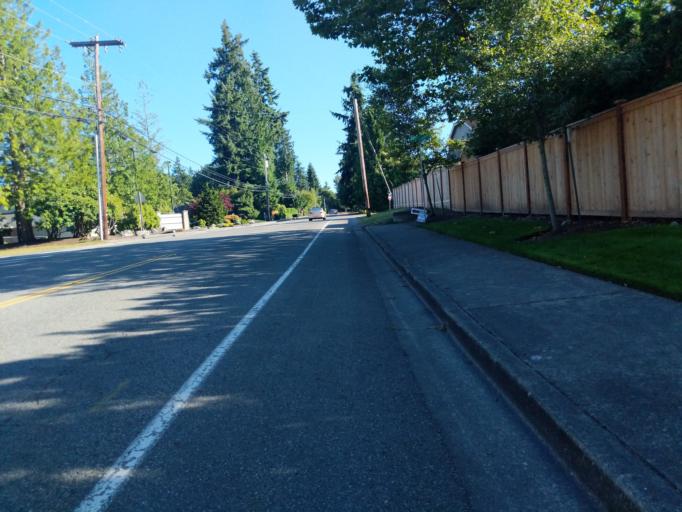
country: US
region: Washington
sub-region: King County
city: Bothell
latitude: 47.7804
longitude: -122.2020
